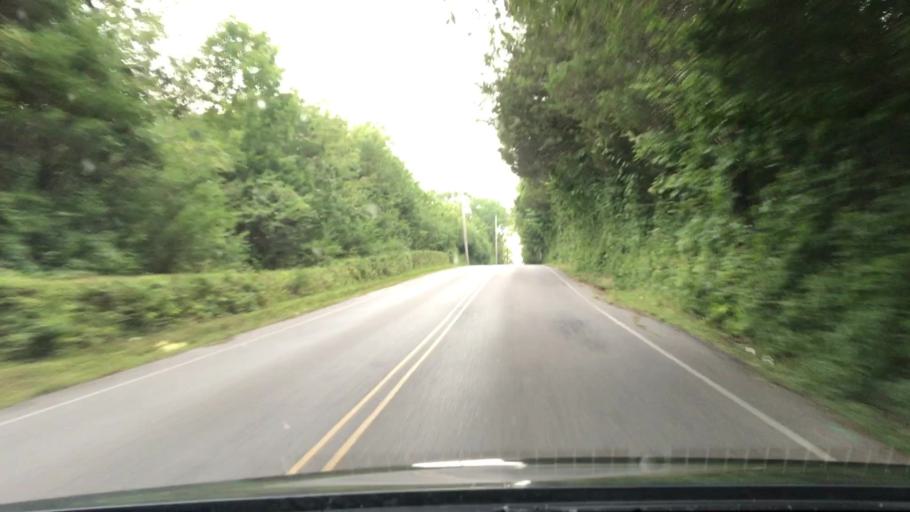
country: US
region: Tennessee
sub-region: Williamson County
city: Nolensville
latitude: 35.9689
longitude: -86.6258
